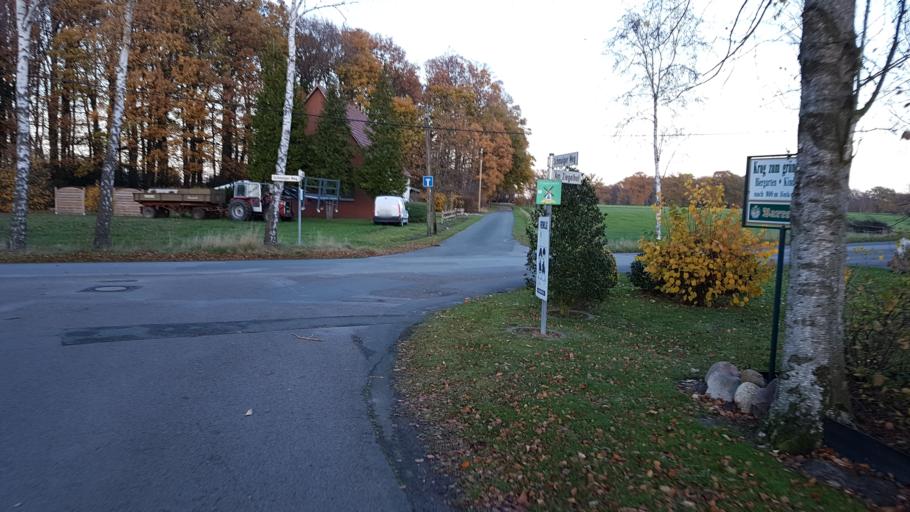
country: DE
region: North Rhine-Westphalia
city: Espelkamp
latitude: 52.4102
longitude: 8.6518
